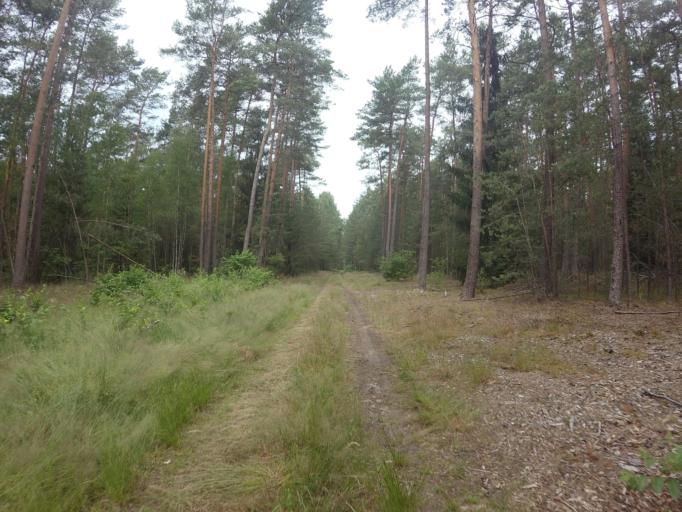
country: PL
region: West Pomeranian Voivodeship
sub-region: Powiat choszczenski
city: Bierzwnik
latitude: 53.1047
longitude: 15.6806
